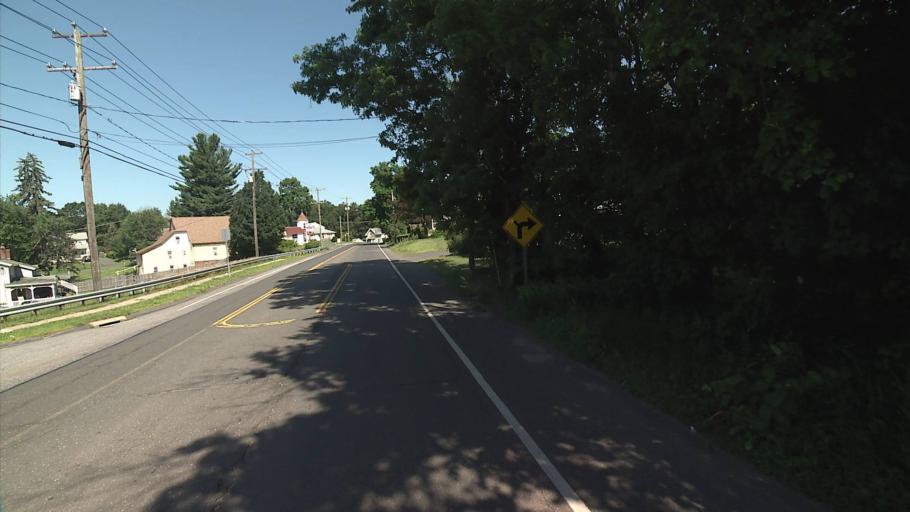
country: US
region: Connecticut
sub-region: Litchfield County
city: Terryville
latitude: 41.6702
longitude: -72.9906
